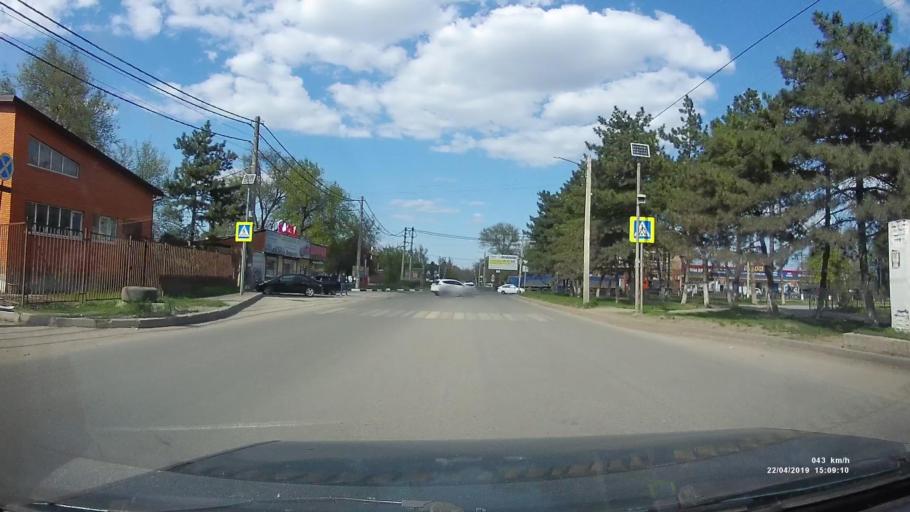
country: RU
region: Rostov
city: Azov
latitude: 47.0992
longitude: 39.4109
